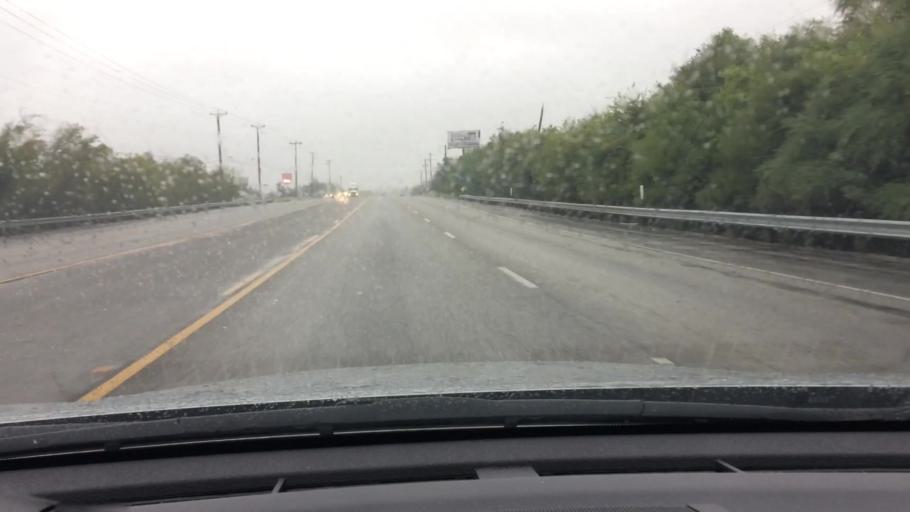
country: US
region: Texas
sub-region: Bexar County
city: Kirby
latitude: 29.4780
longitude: -98.3662
